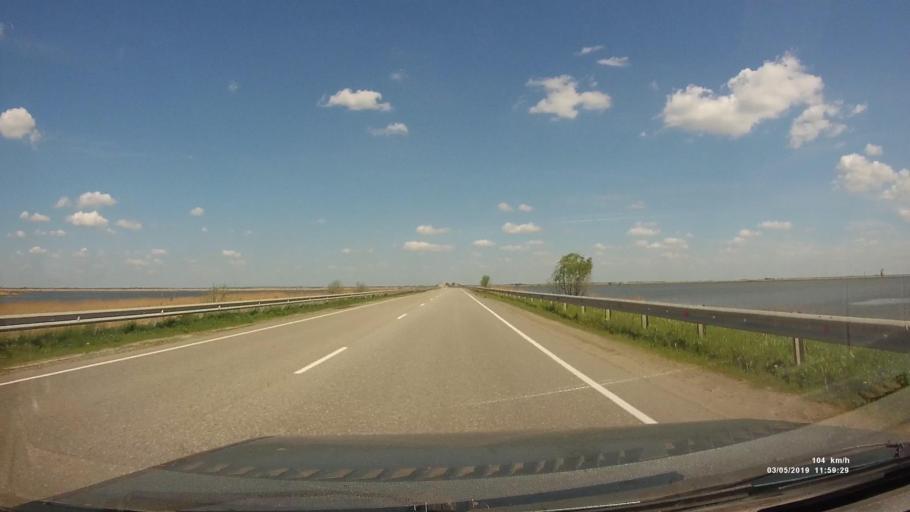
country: RU
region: Rostov
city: Bagayevskaya
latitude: 47.2355
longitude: 40.3308
